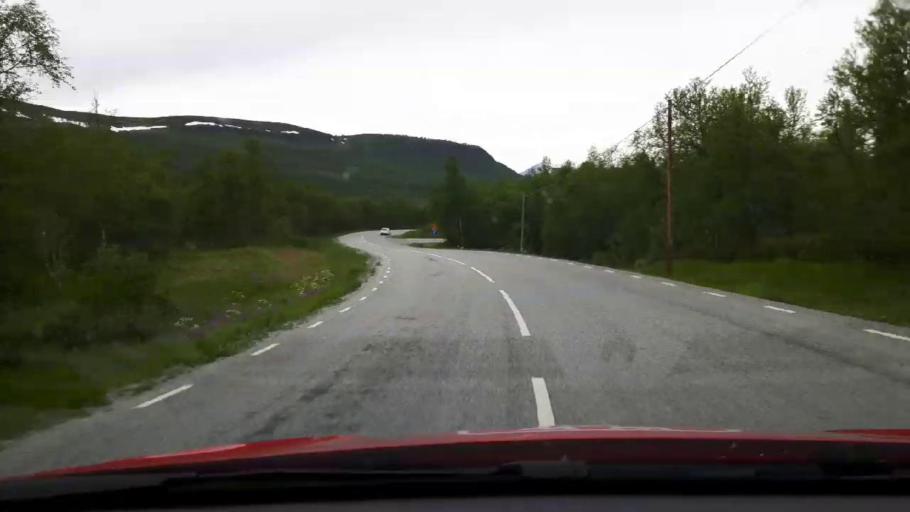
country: NO
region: Sor-Trondelag
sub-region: Tydal
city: Aas
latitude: 62.6724
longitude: 12.4292
